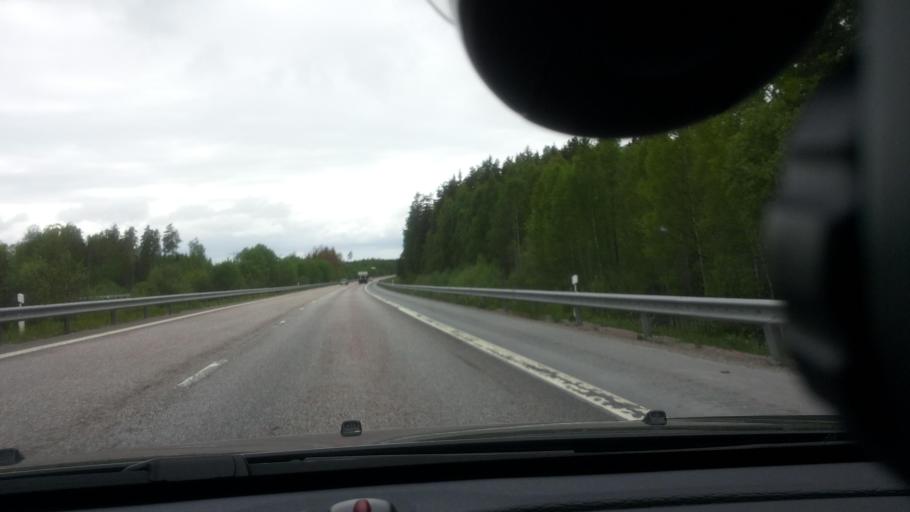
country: SE
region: Uppsala
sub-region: Alvkarleby Kommun
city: AElvkarleby
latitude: 60.4730
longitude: 17.3875
